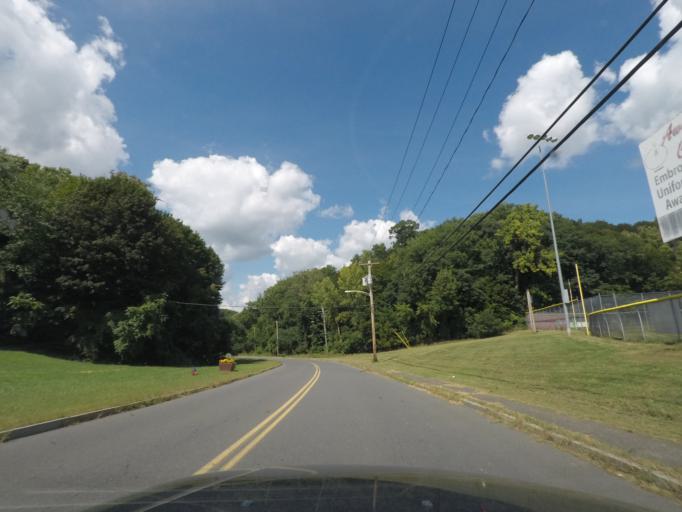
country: US
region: New York
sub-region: Rensselaer County
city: Troy
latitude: 42.7136
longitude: -73.6713
